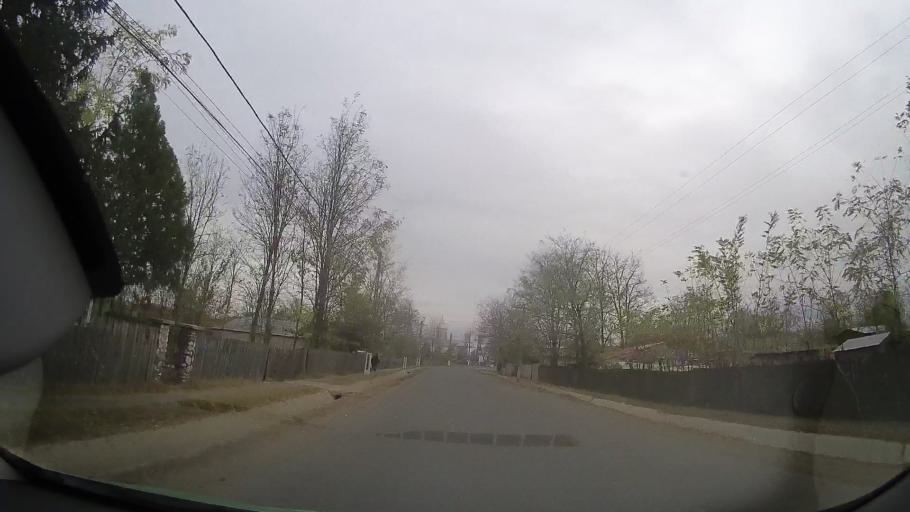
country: RO
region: Braila
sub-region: Comuna Rosiori
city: Rosiori
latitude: 44.8069
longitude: 27.3807
